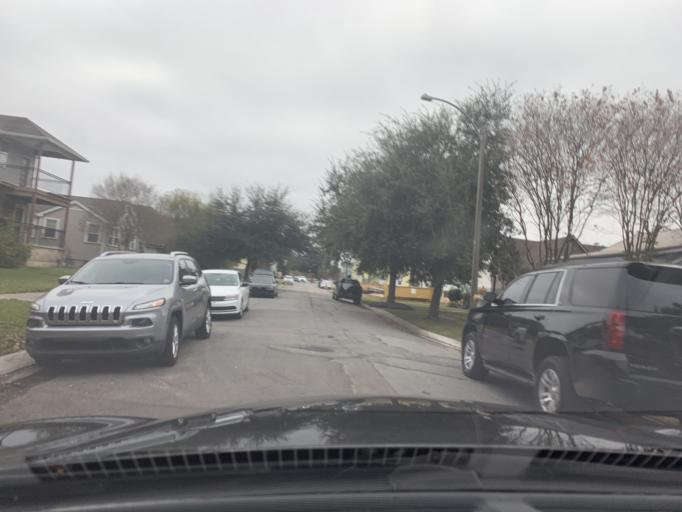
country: US
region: Louisiana
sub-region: Jefferson Parish
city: Metairie
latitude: 30.0063
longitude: -90.1112
